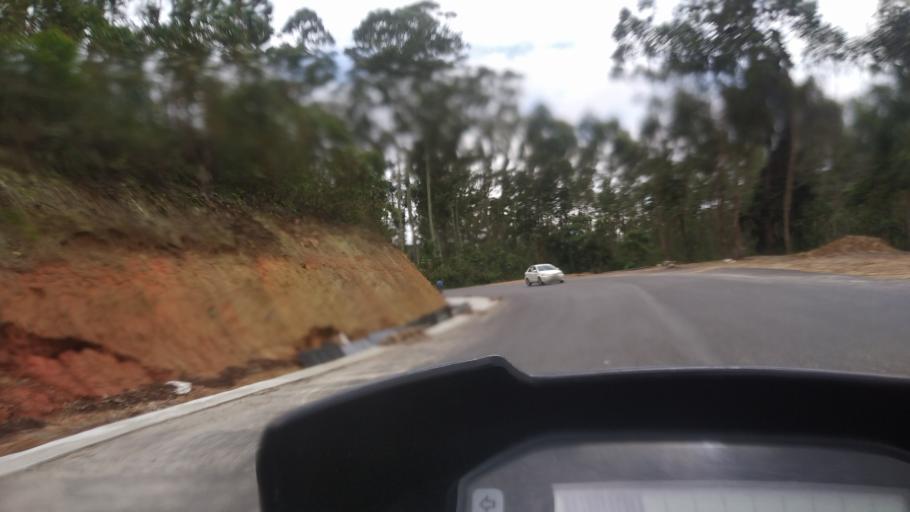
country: IN
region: Kerala
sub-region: Idukki
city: Munnar
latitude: 10.0720
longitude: 77.0941
